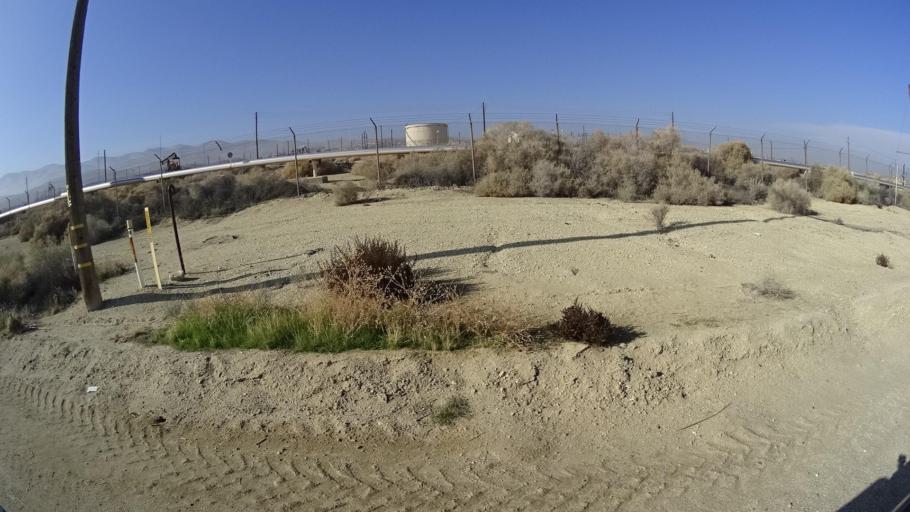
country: US
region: California
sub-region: Kern County
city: Taft Heights
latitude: 35.2125
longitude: -119.5982
